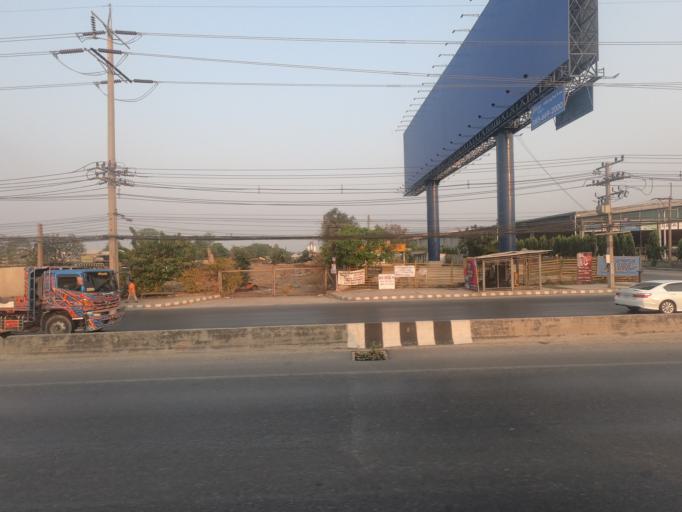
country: TH
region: Pathum Thani
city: Khlong Luang
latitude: 14.0445
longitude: 100.6167
